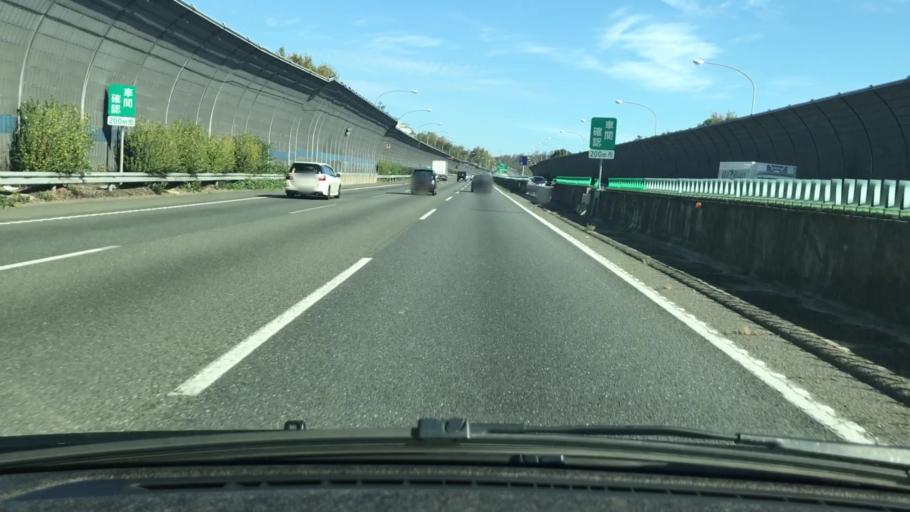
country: JP
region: Osaka
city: Ibaraki
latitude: 34.8481
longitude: 135.5790
